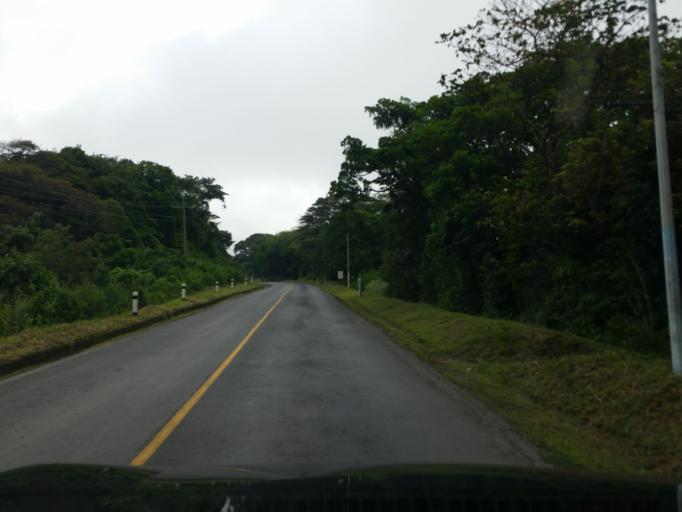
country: NI
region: Managua
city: El Crucero
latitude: 12.0102
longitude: -86.3192
